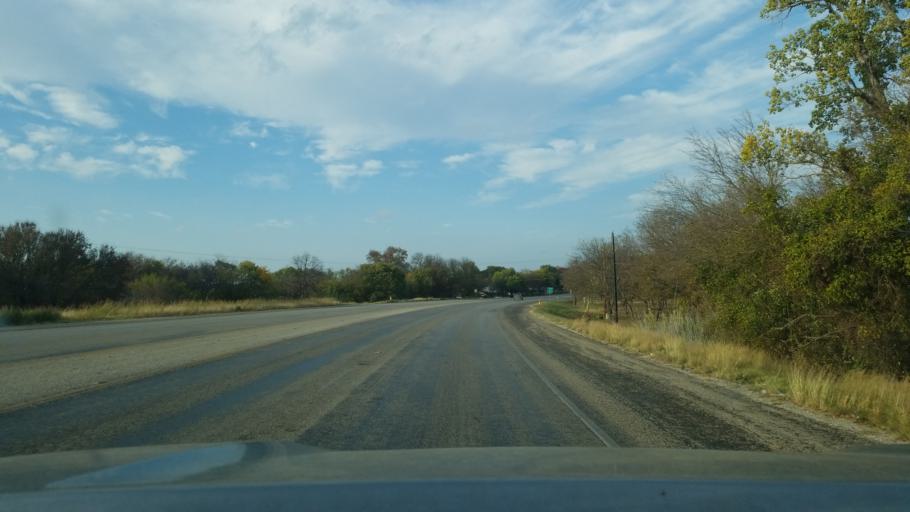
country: US
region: Texas
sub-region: Brown County
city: Early
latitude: 31.7451
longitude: -98.9644
